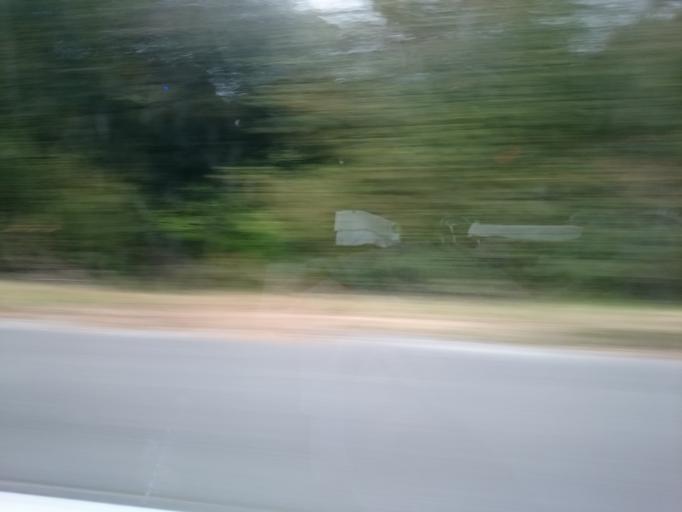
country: FR
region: Brittany
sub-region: Departement du Finistere
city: Mellac
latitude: 47.8726
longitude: -3.6037
